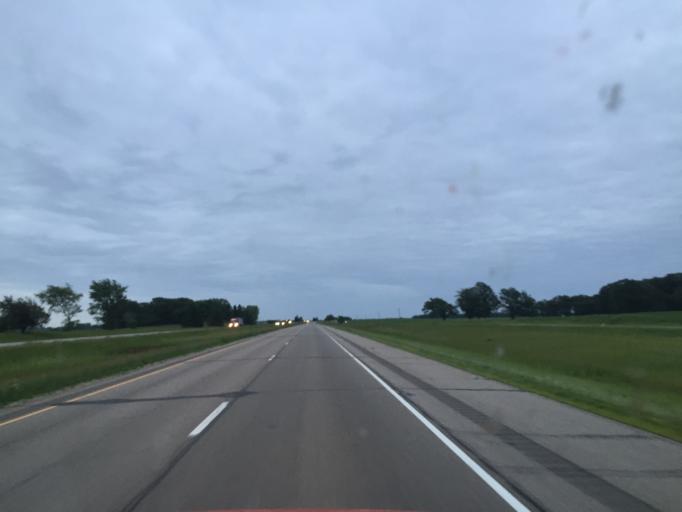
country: US
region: Minnesota
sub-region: Mower County
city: Austin
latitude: 43.6590
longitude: -93.0827
